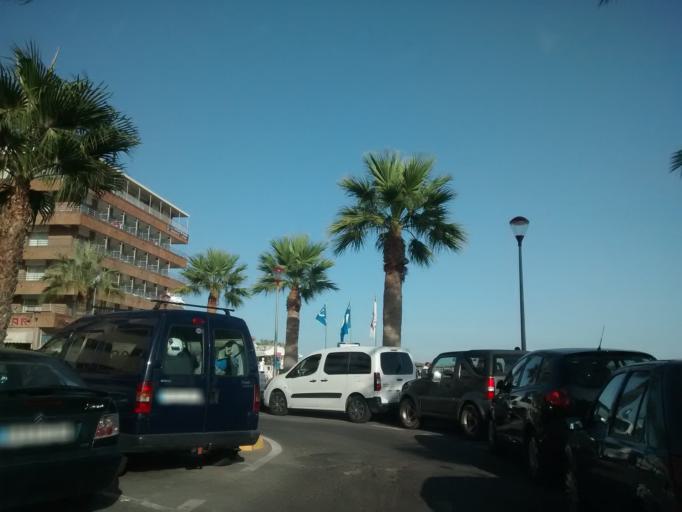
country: ES
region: Valencia
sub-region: Provincia de Alicante
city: Santa Pola
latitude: 38.1897
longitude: -0.5560
